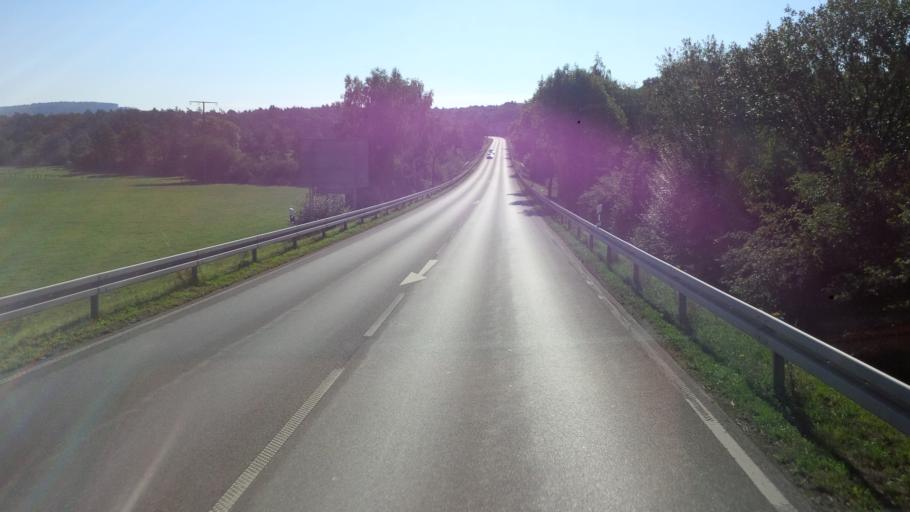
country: DE
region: Hesse
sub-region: Regierungsbezirk Darmstadt
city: Wehrheim
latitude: 50.2839
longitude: 8.5489
